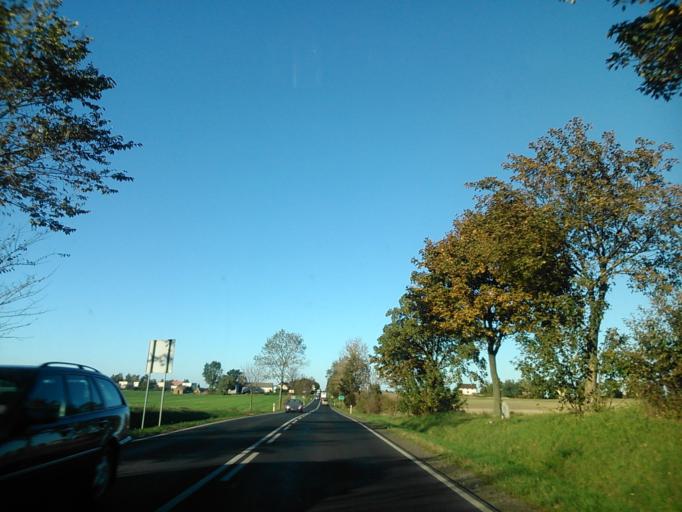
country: PL
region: Kujawsko-Pomorskie
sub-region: Powiat torunski
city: Lubicz Gorny
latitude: 53.0829
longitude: 18.7685
